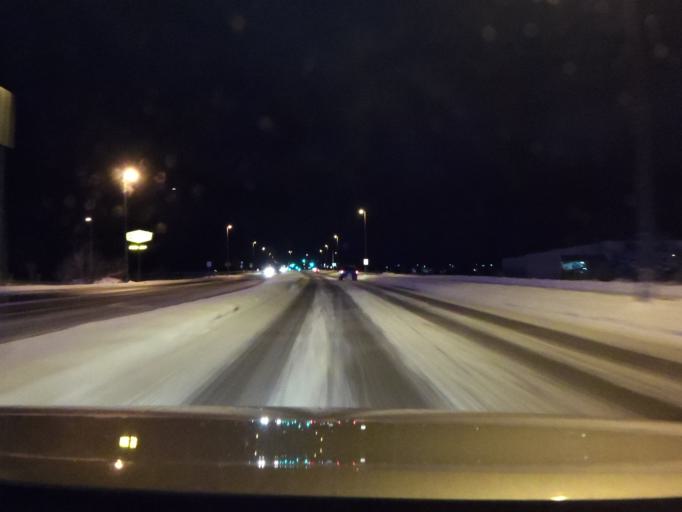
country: US
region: Wisconsin
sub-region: Dunn County
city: Menomonie
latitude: 44.9033
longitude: -91.9321
